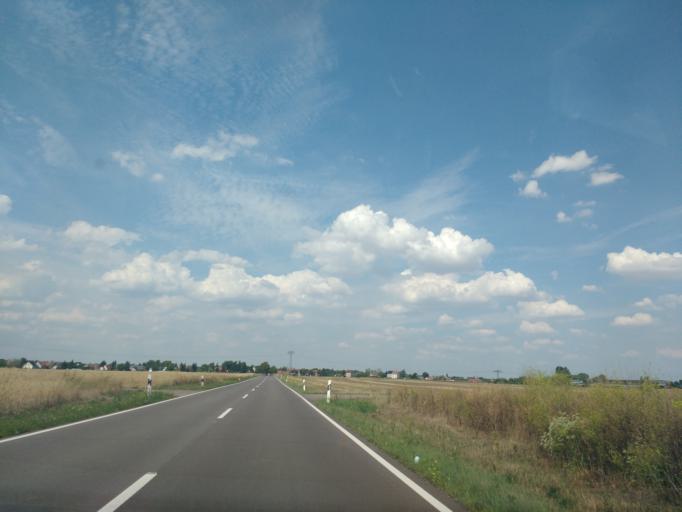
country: DE
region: Saxony-Anhalt
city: Dolbau
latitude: 51.4650
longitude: 12.0480
